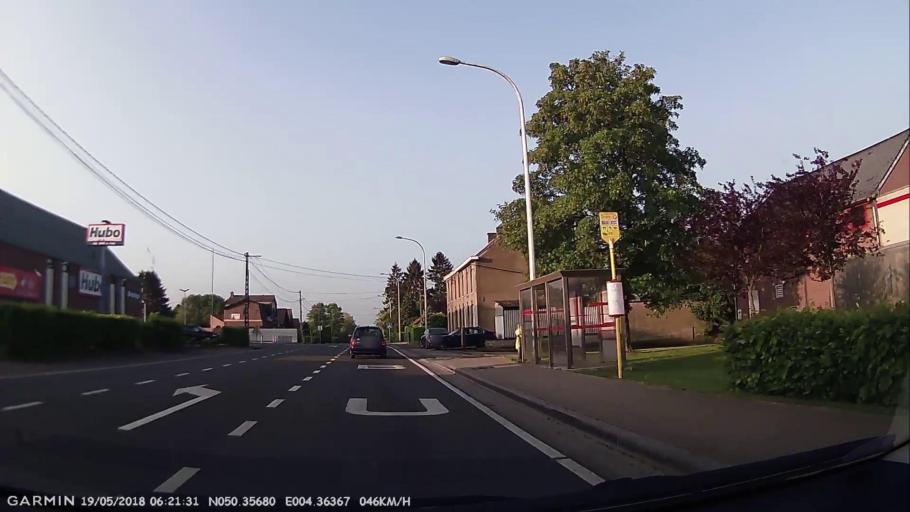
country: BE
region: Wallonia
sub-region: Province du Hainaut
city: Thuin
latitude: 50.3567
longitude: 4.3637
